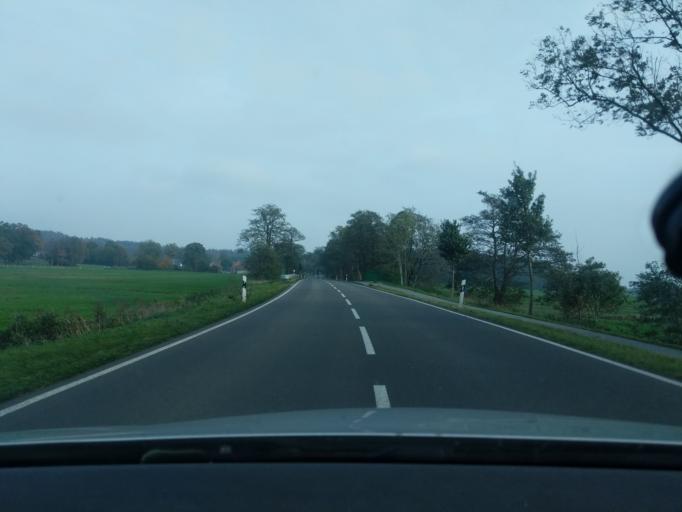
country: DE
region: Lower Saxony
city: Kranenburg
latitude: 53.6236
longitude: 9.1757
